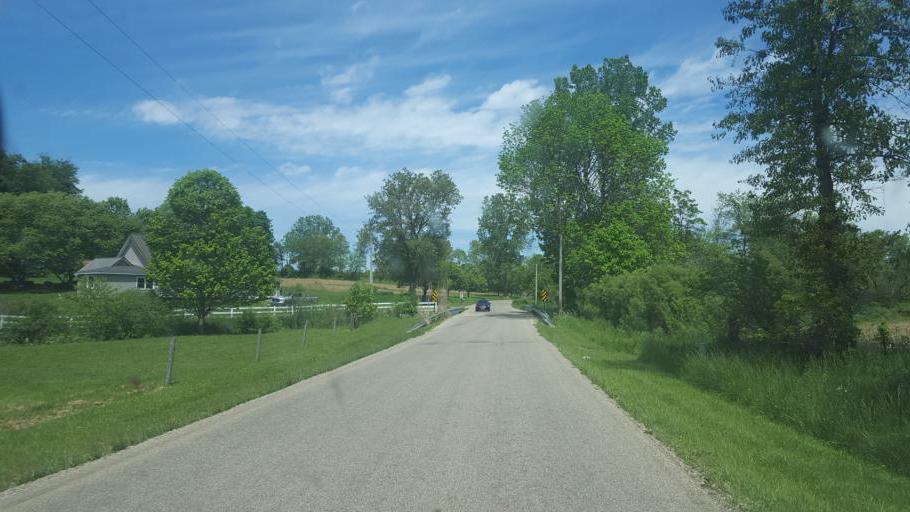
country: US
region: Ohio
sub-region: Knox County
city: Oak Hill
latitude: 40.3784
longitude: -82.3139
